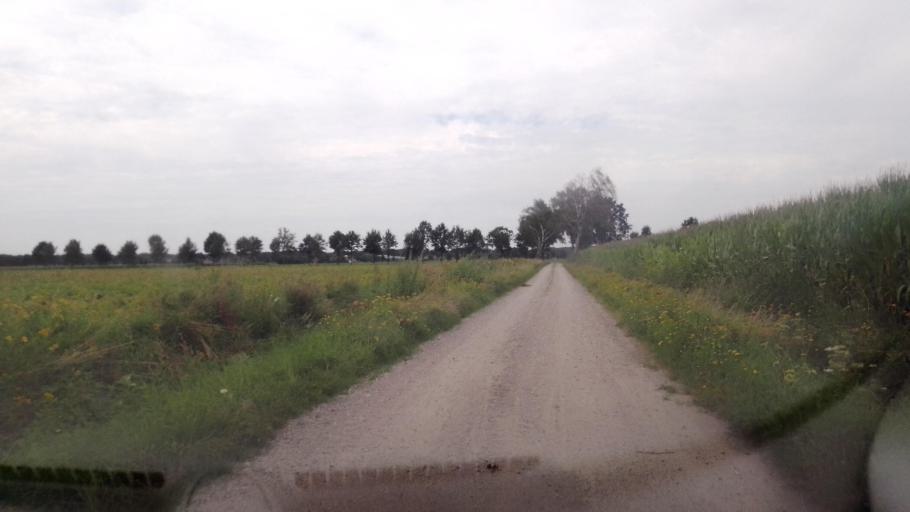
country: NL
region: Limburg
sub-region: Gemeente Peel en Maas
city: Maasbree
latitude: 51.3881
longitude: 6.0170
